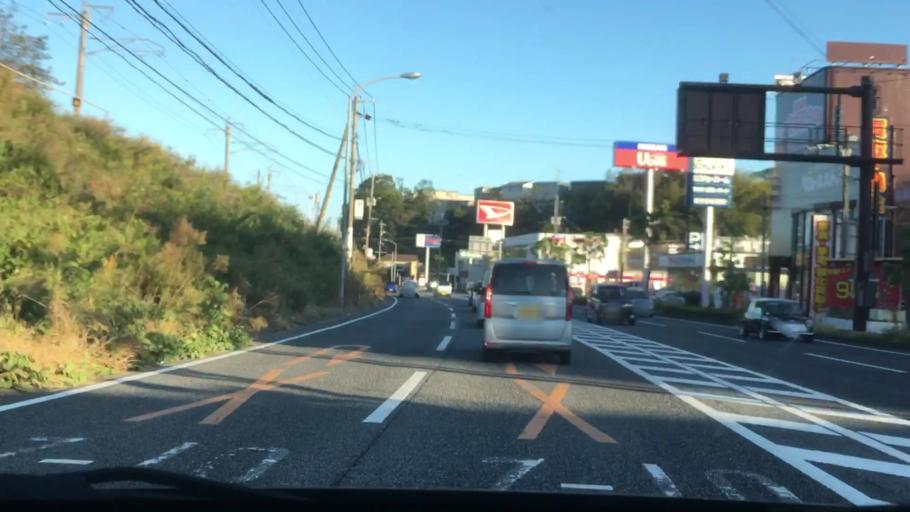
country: JP
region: Nagasaki
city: Sasebo
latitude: 33.1538
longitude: 129.7738
